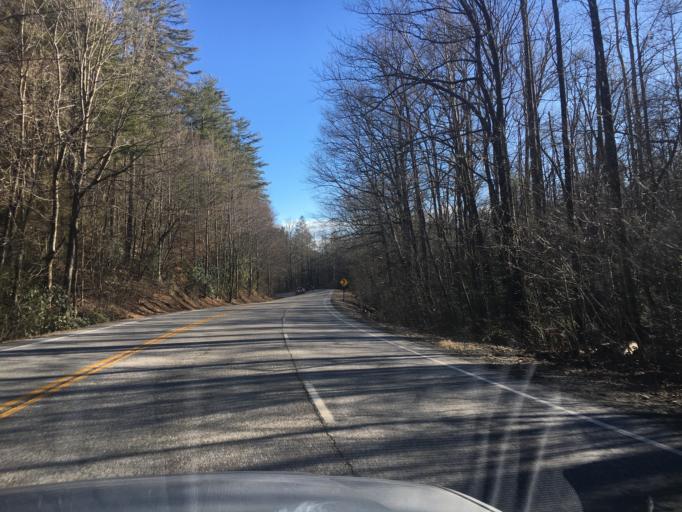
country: US
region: Georgia
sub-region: Lumpkin County
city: Dahlonega
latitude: 34.6988
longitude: -83.9143
